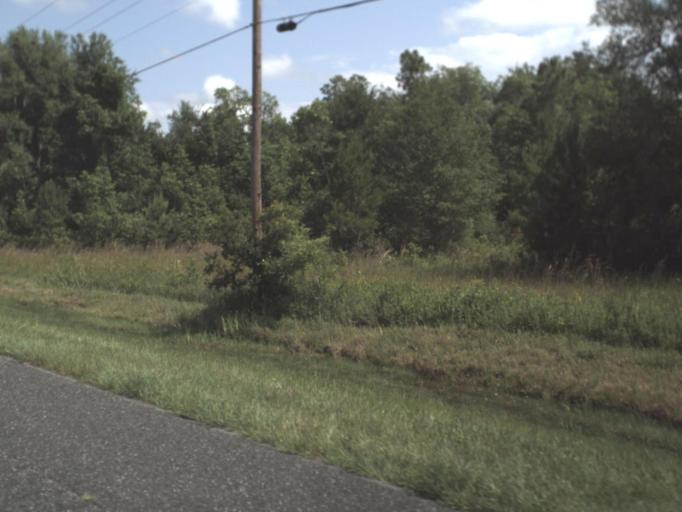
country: US
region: Florida
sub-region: Alachua County
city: Gainesville
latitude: 29.5161
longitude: -82.2941
